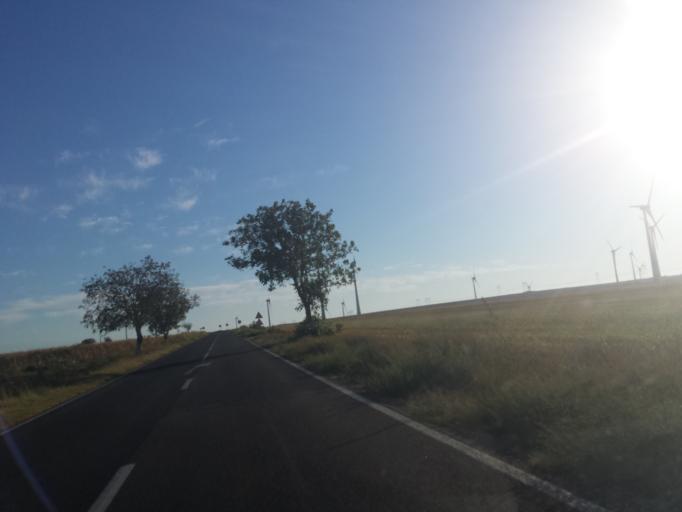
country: RO
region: Constanta
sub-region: Comuna Saraiu
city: Saraiu
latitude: 44.7725
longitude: 28.2201
